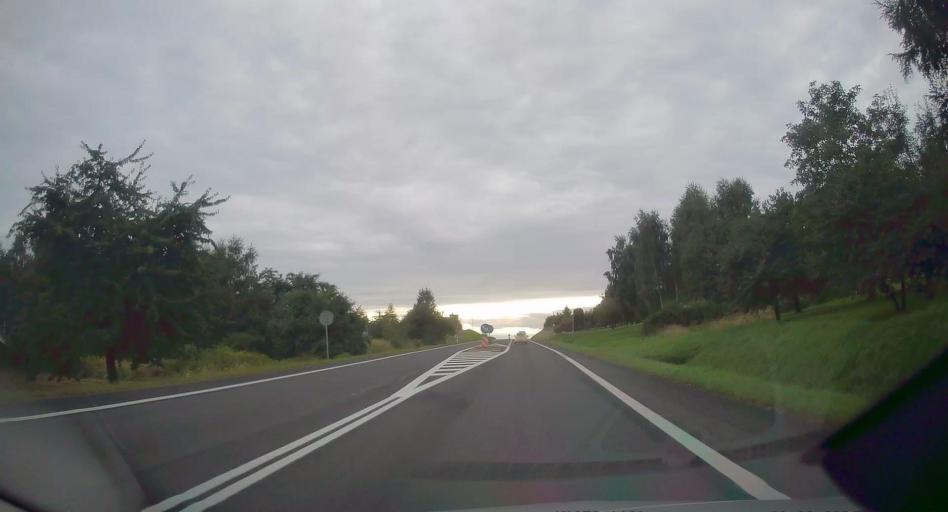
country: PL
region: Lesser Poland Voivodeship
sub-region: Powiat wielicki
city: Trabki
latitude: 49.9833
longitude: 20.1380
